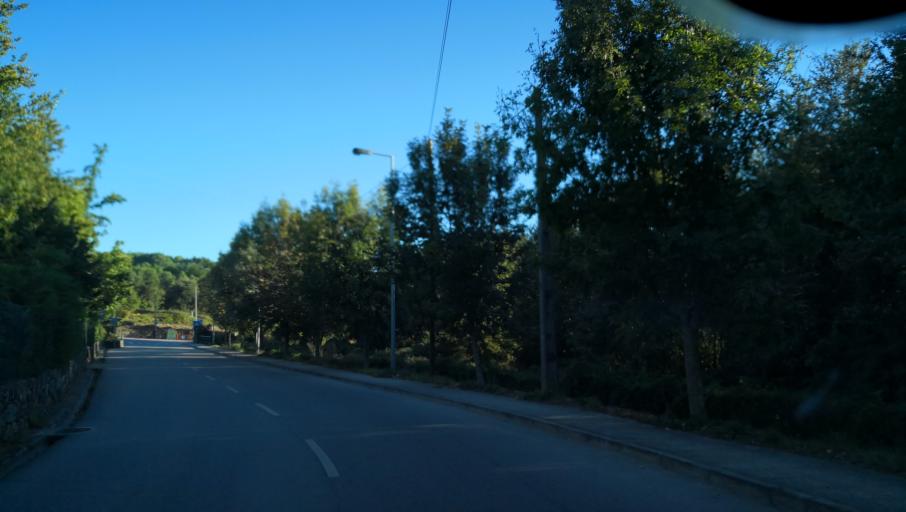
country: PT
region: Vila Real
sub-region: Vila Real
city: Vila Real
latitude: 41.3189
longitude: -7.7428
